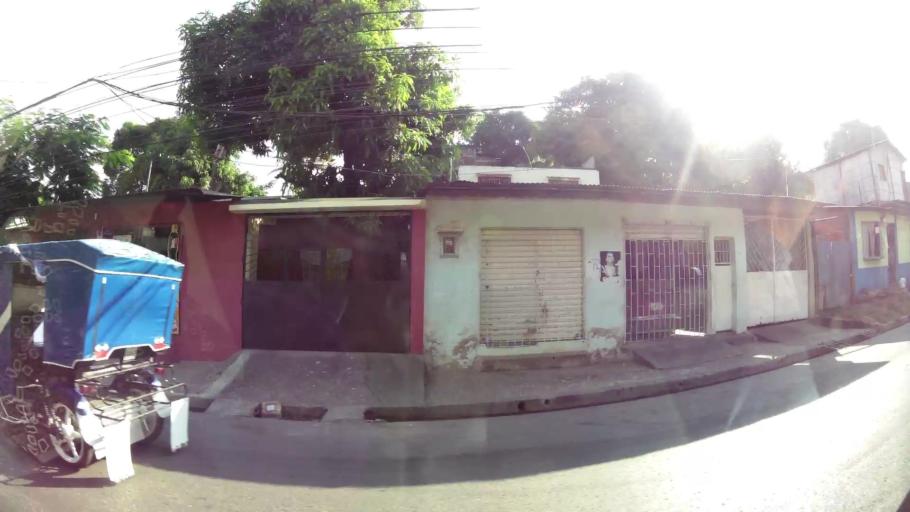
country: EC
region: Guayas
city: Eloy Alfaro
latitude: -2.0763
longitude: -79.9324
